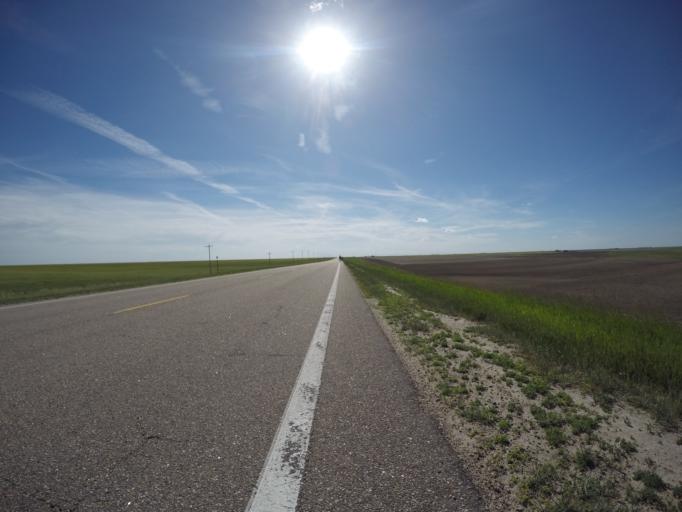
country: US
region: Kansas
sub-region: Cheyenne County
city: Saint Francis
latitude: 39.7566
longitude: -101.9956
